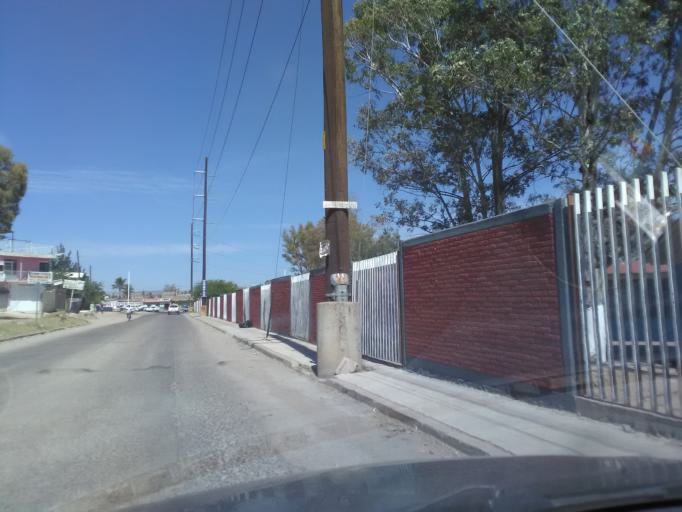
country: MX
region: Durango
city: Victoria de Durango
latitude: 24.0093
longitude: -104.6327
